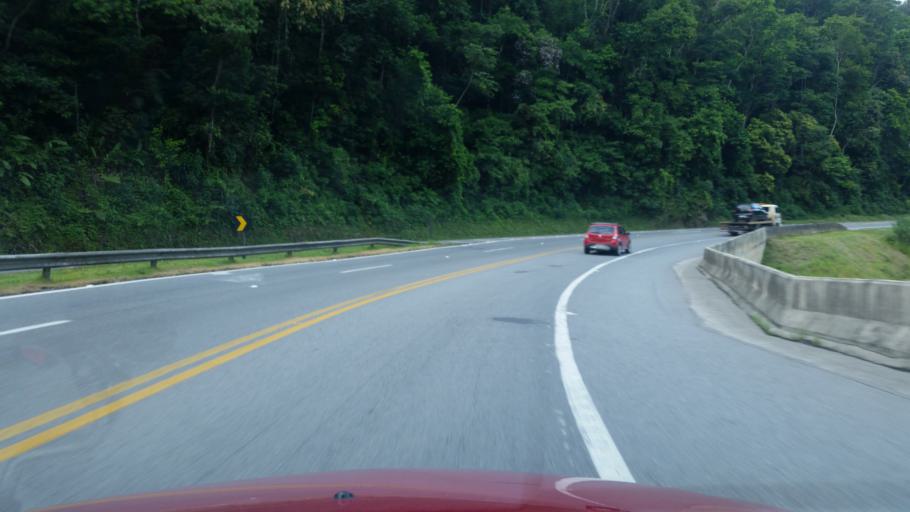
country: BR
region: Sao Paulo
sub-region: Miracatu
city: Miracatu
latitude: -24.2674
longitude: -47.2826
